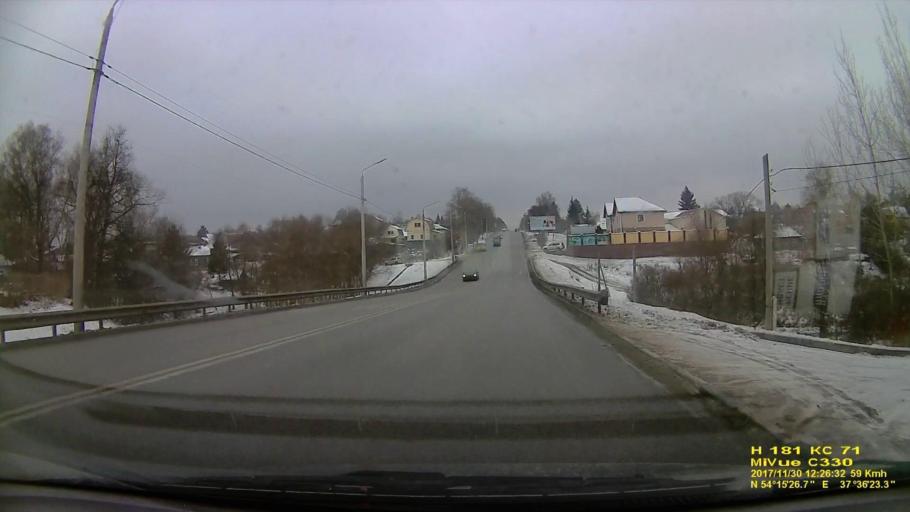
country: RU
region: Tula
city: Gorelki
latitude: 54.2575
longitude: 37.6064
